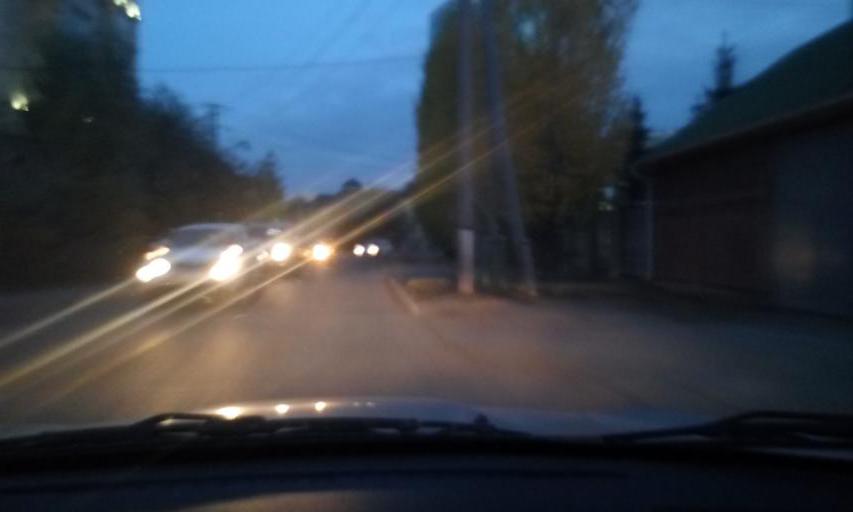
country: KZ
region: Astana Qalasy
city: Astana
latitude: 51.1371
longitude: 71.4296
